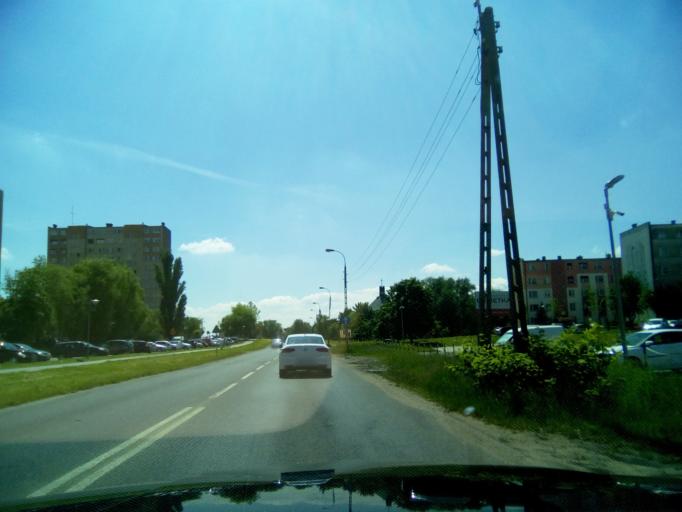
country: PL
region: Greater Poland Voivodeship
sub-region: Powiat gnieznienski
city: Gniezno
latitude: 52.5523
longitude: 17.6046
